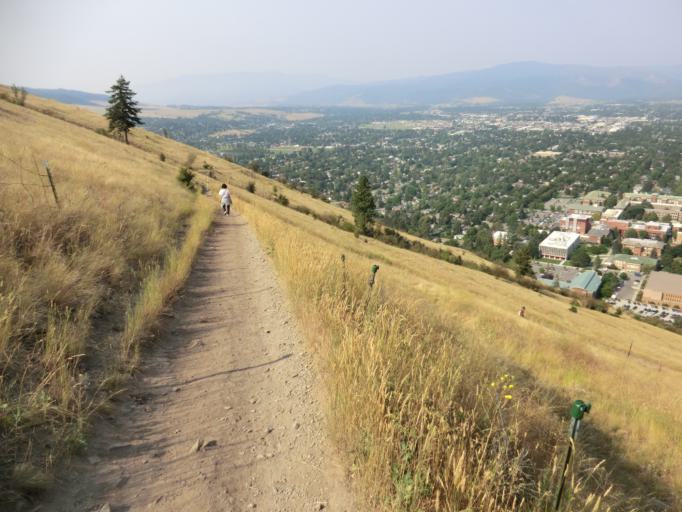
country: US
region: Montana
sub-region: Missoula County
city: Missoula
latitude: 46.8594
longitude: -113.9762
